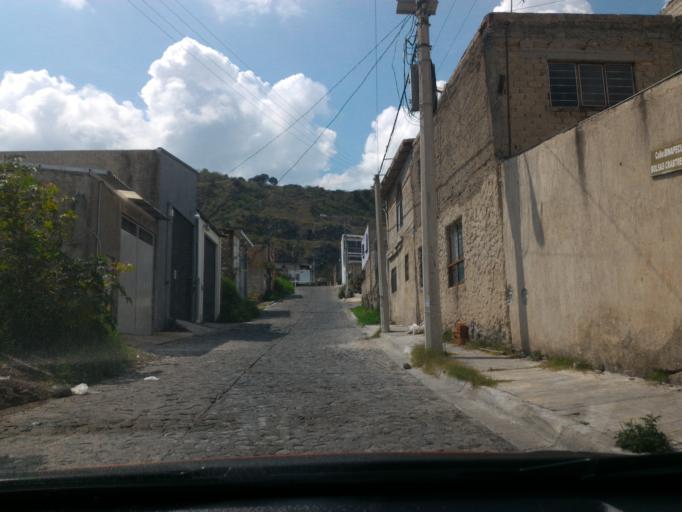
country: MX
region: Jalisco
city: Guadalajara
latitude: 20.6614
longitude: -103.4539
